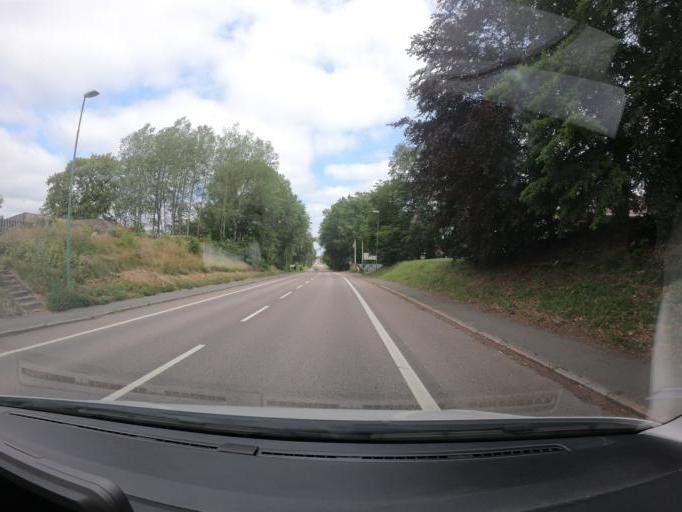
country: SE
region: Skane
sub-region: Hassleholms Kommun
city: Tormestorp
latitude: 56.1631
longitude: 13.5918
